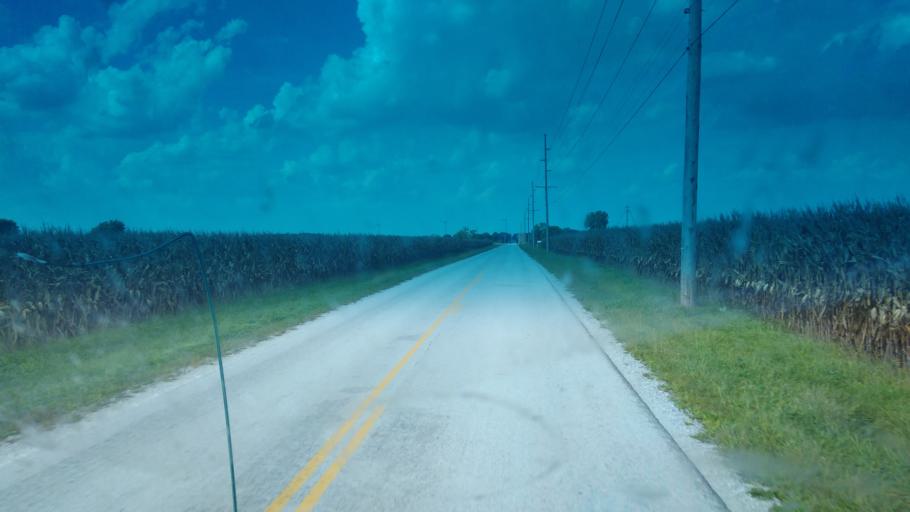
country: US
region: Ohio
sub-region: Hancock County
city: Arlington
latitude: 40.7670
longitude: -83.6522
